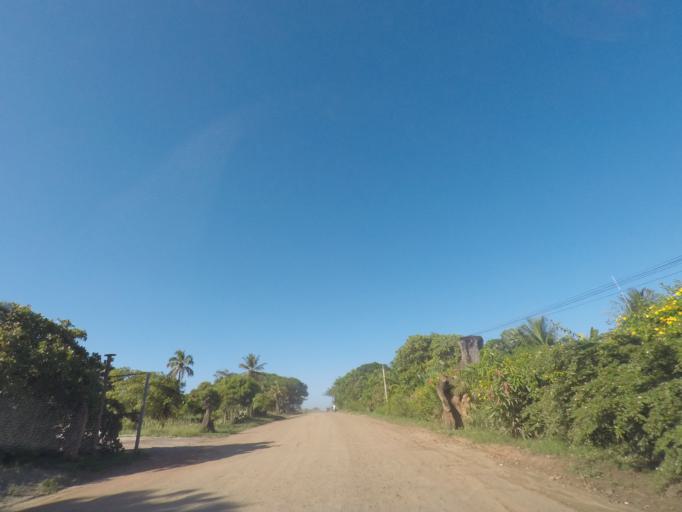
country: BR
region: Bahia
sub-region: Marau
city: Marau
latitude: -14.0392
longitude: -38.9553
